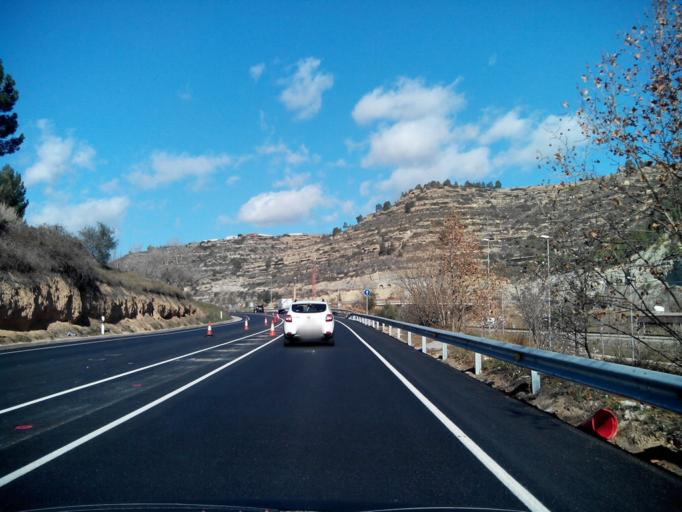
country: ES
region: Catalonia
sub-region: Provincia de Barcelona
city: Manresa
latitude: 41.7025
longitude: 1.8414
